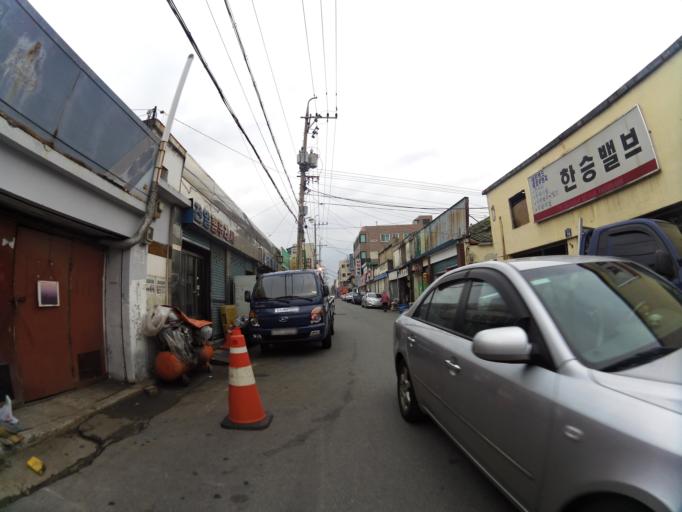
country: KR
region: Daegu
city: Daegu
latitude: 35.8722
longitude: 128.5863
